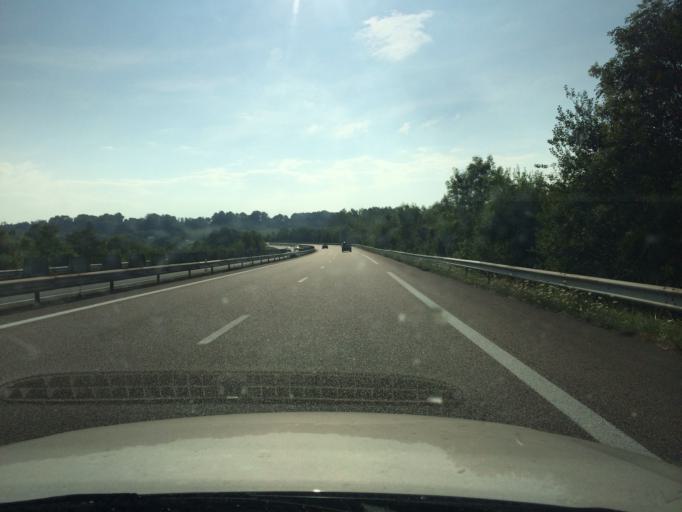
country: FR
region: Haute-Normandie
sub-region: Departement de l'Eure
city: Toutainville
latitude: 49.3499
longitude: 0.4362
